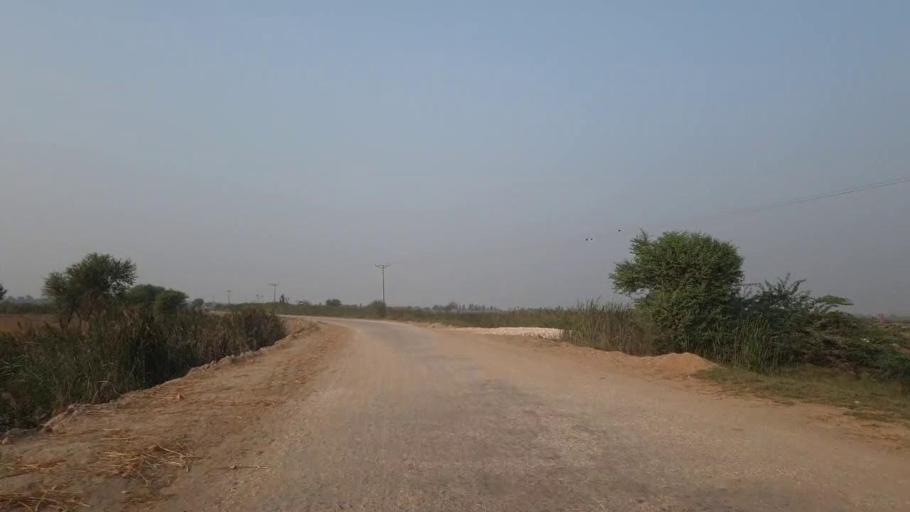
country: PK
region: Sindh
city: Tando Muhammad Khan
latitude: 25.1039
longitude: 68.4308
